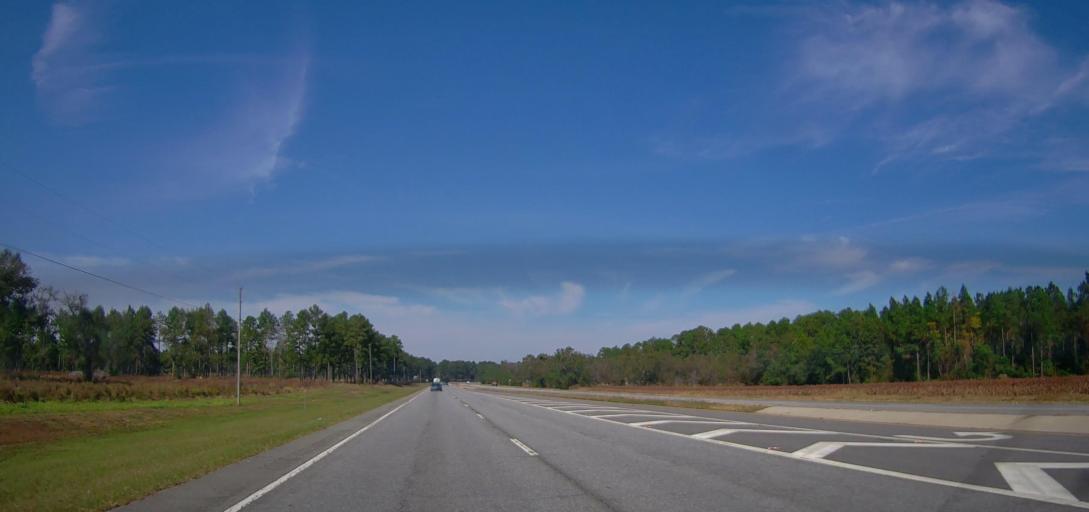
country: US
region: Georgia
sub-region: Lee County
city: Leesburg
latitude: 31.7441
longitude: -83.9873
